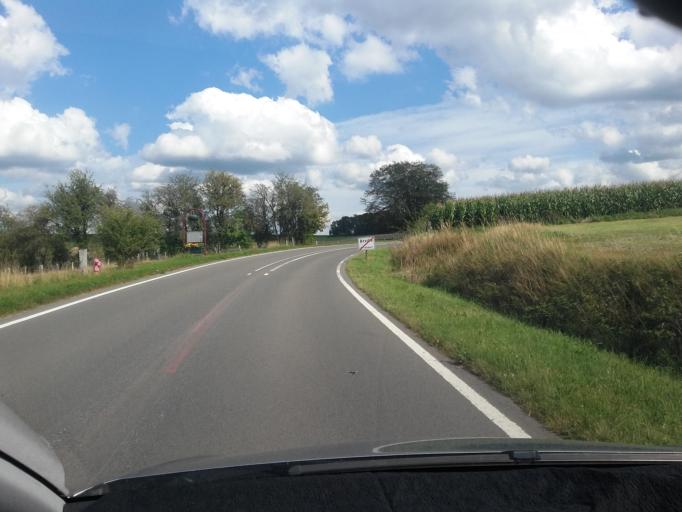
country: BE
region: Wallonia
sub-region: Province du Luxembourg
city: Saint-Hubert
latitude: 50.0318
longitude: 5.3287
